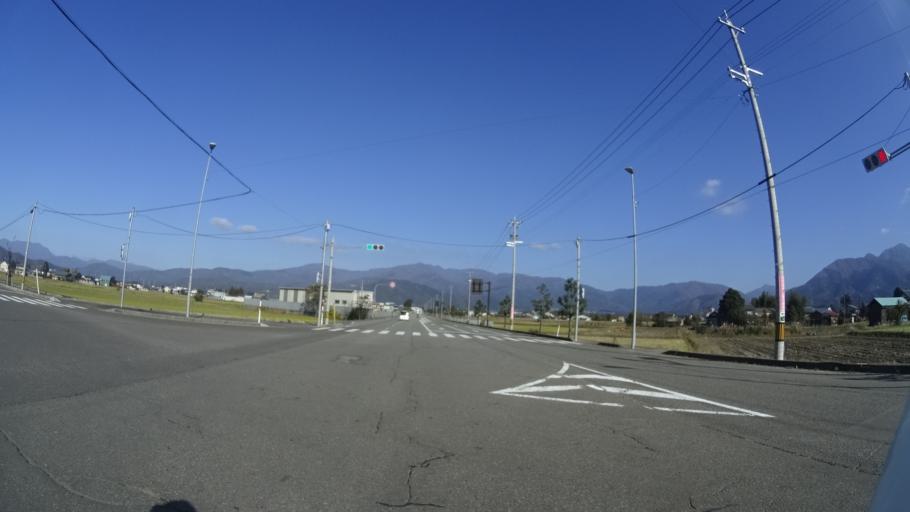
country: JP
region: Fukui
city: Ono
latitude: 35.9749
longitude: 136.5119
